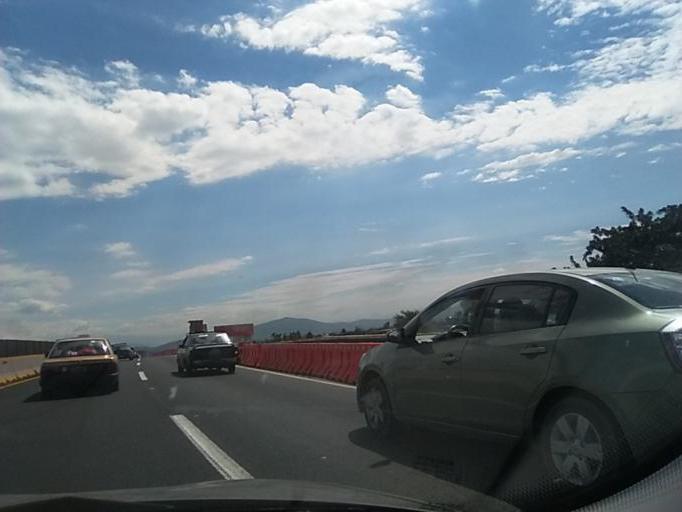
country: MX
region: Morelos
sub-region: Cuernavaca
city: Colonia los Cerritos
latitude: 18.9603
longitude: -99.2173
